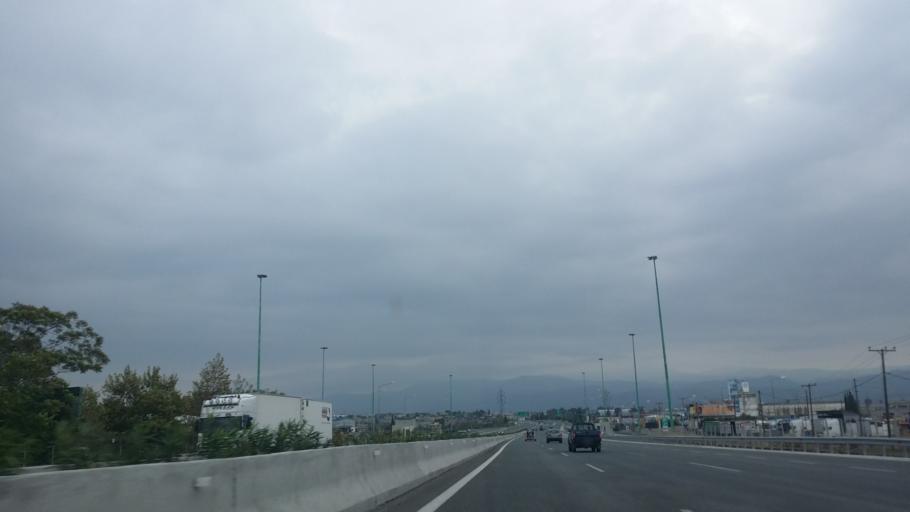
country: GR
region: Central Greece
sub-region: Nomos Voiotias
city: Schimatari
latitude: 38.3366
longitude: 23.5979
